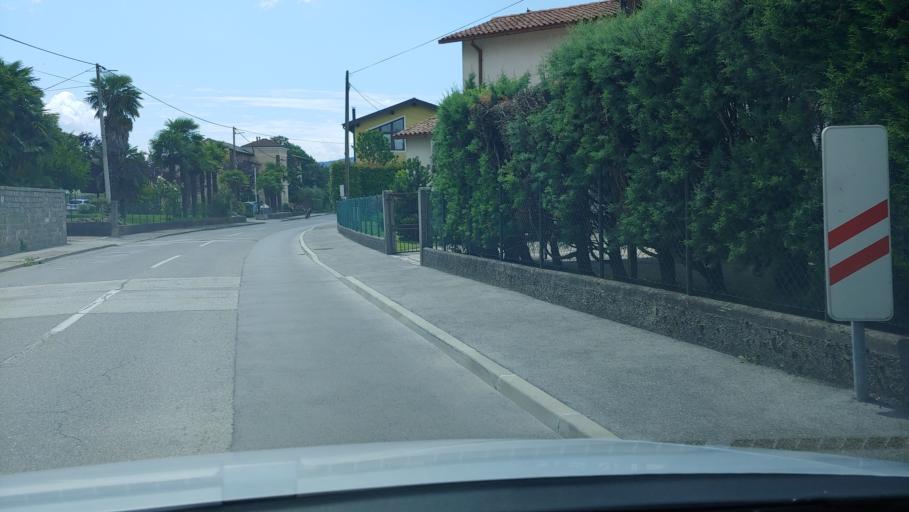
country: SI
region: Sempeter-Vrtojba
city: Sempeter pri Gorici
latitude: 45.9274
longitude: 13.6406
